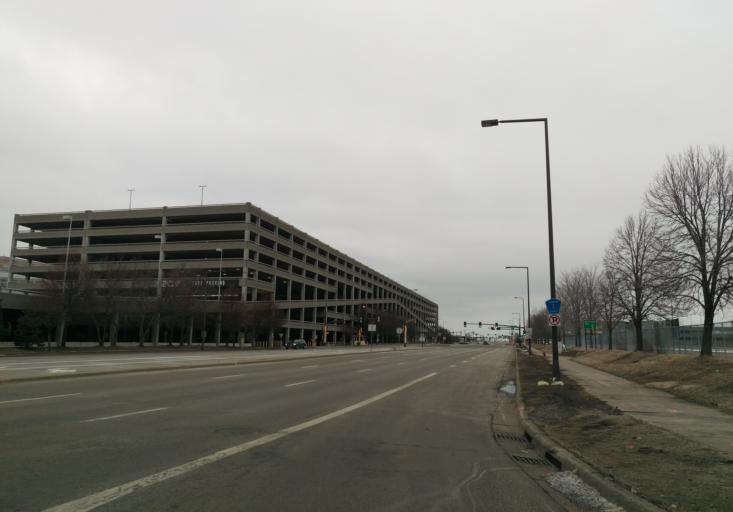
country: US
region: Minnesota
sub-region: Hennepin County
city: Richfield
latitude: 44.8523
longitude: -93.2374
